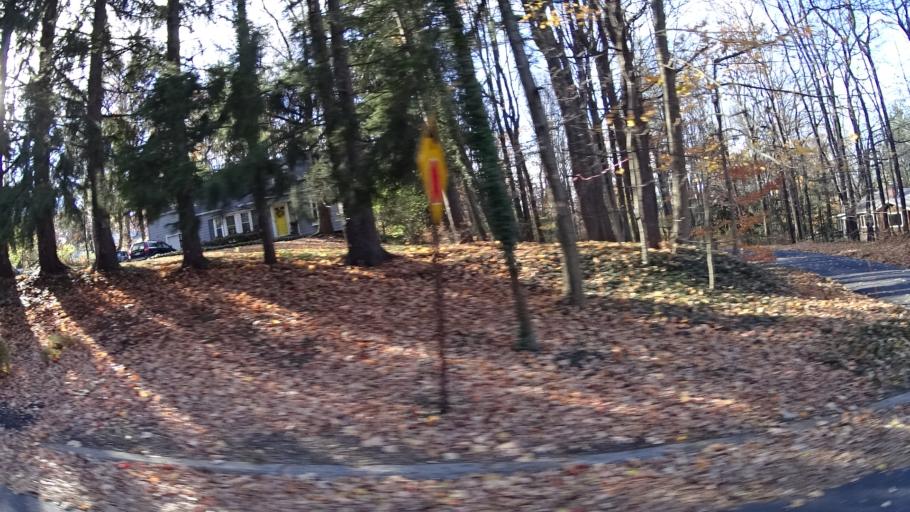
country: US
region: New Jersey
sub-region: Union County
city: Berkeley Heights
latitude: 40.6846
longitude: -74.4807
